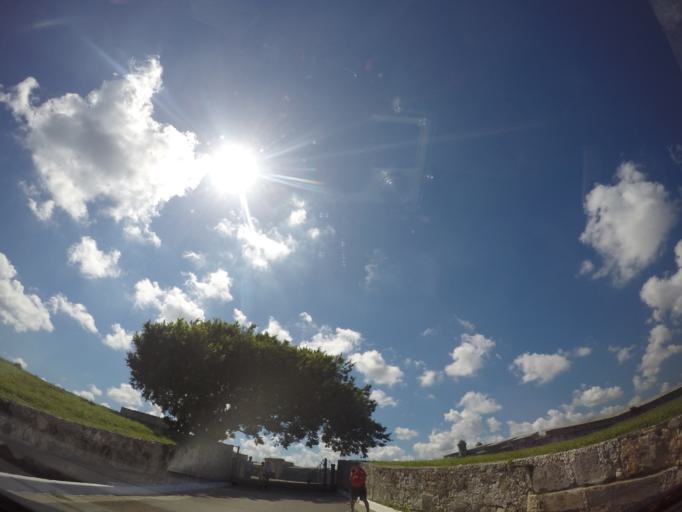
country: CU
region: La Habana
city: Centro Habana
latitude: 23.1487
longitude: -82.3508
